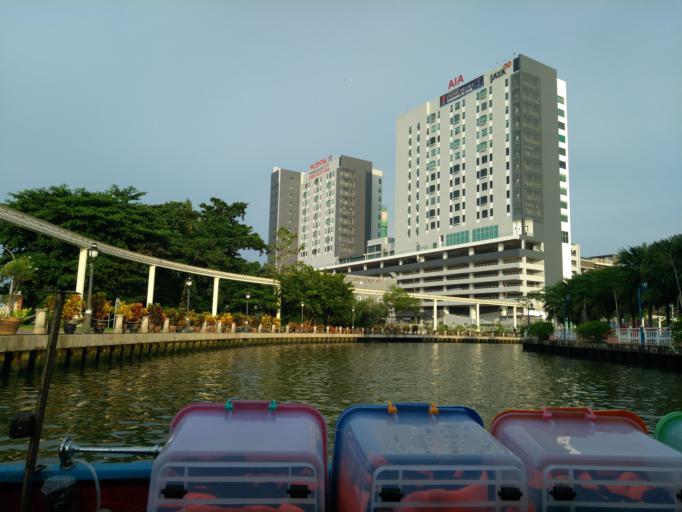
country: MY
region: Melaka
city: Malacca
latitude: 2.2061
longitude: 102.2507
